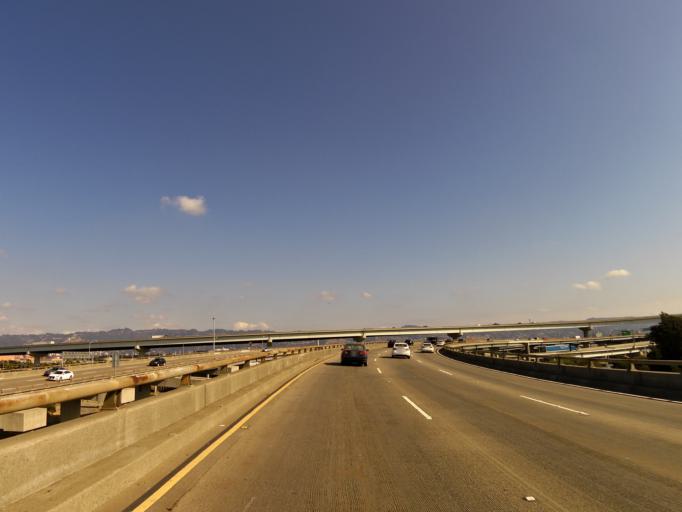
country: US
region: California
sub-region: Alameda County
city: Emeryville
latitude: 37.8270
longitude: -122.2956
